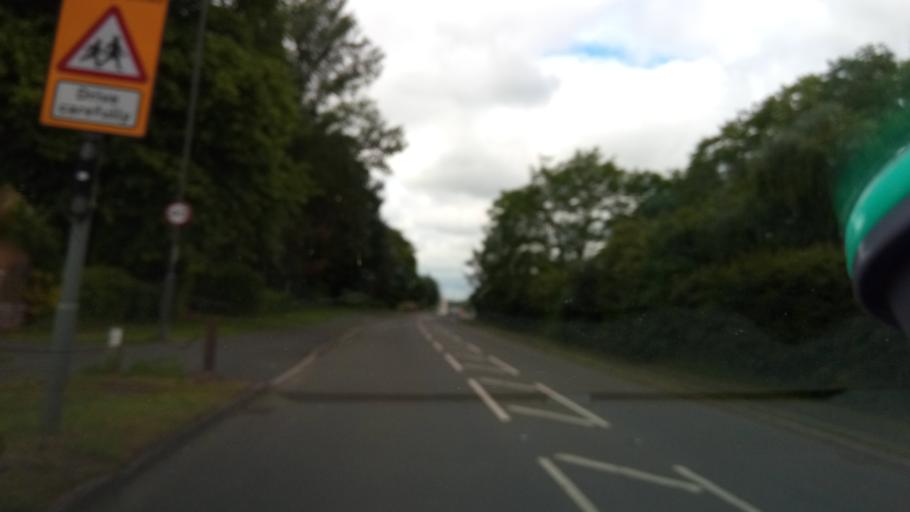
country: GB
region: England
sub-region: Derbyshire
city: Repton
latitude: 52.8533
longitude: -1.5558
